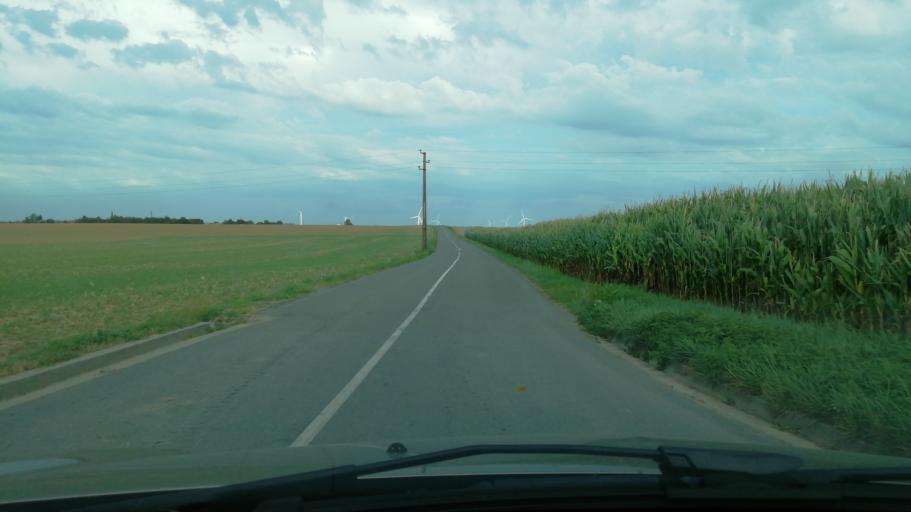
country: FR
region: Nord-Pas-de-Calais
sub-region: Departement du Nord
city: Saint-Hilaire-lez-Cambrai
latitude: 50.1746
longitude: 3.3917
